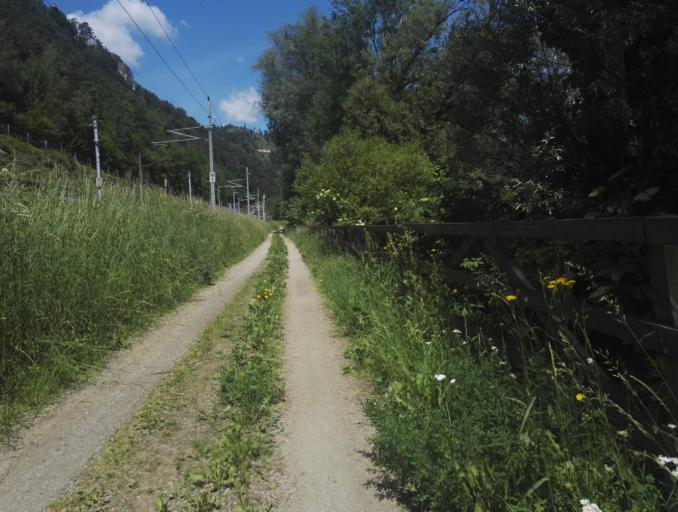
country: AT
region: Styria
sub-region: Politischer Bezirk Graz-Umgebung
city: Gratkorn
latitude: 47.1508
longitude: 15.3227
